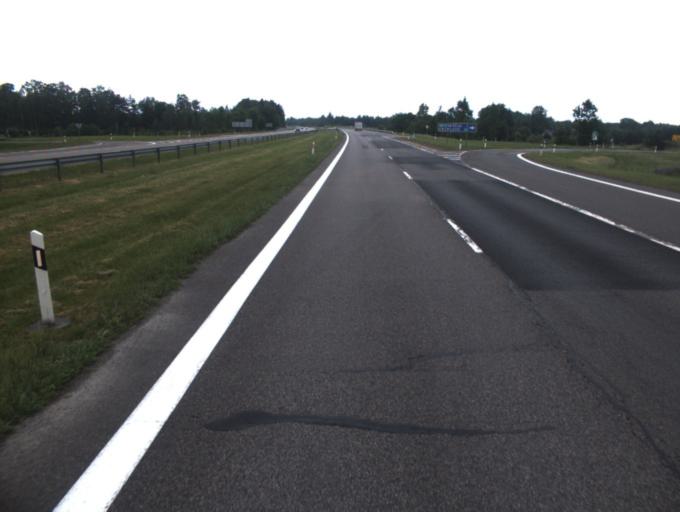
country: LT
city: Skaudvile
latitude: 55.4246
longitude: 22.7627
